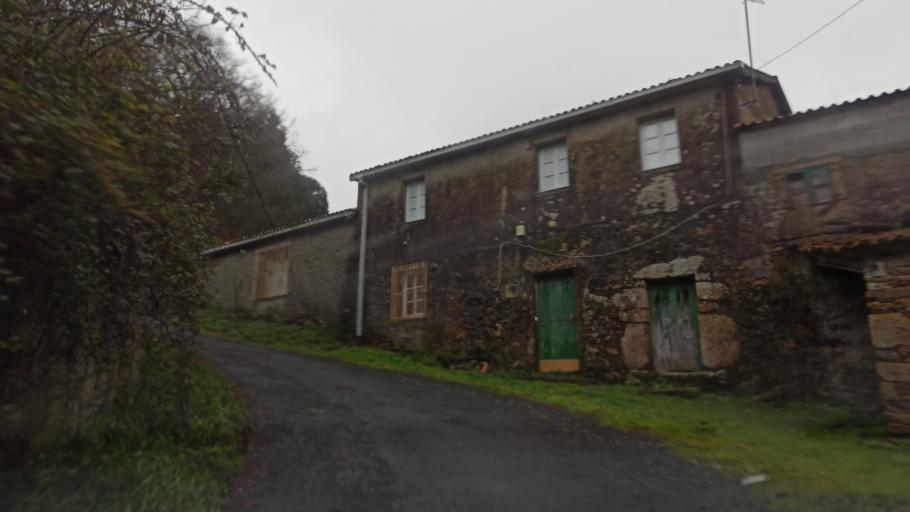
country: ES
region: Galicia
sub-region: Provincia da Coruna
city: Coiros
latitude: 43.1820
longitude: -8.1369
